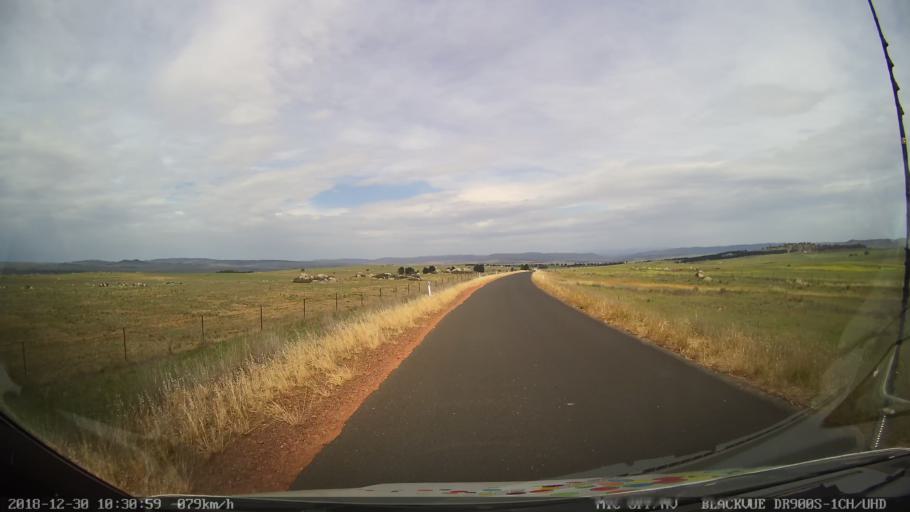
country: AU
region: New South Wales
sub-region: Snowy River
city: Berridale
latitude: -36.5051
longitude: 148.8865
